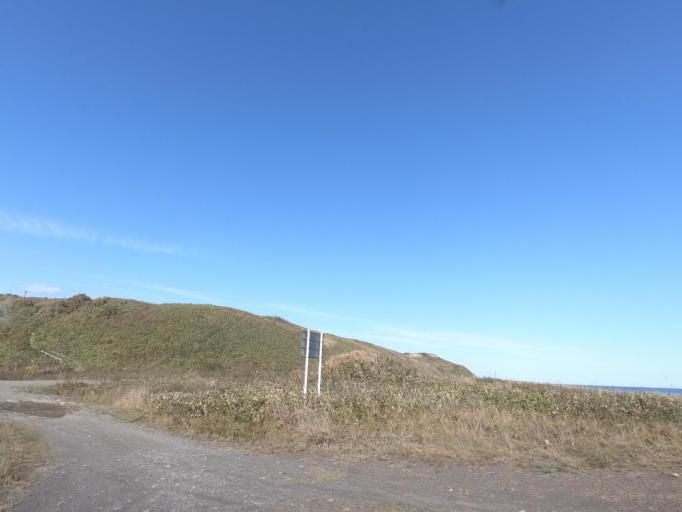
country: JP
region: Hokkaido
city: Obihiro
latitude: 42.6003
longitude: 143.5508
